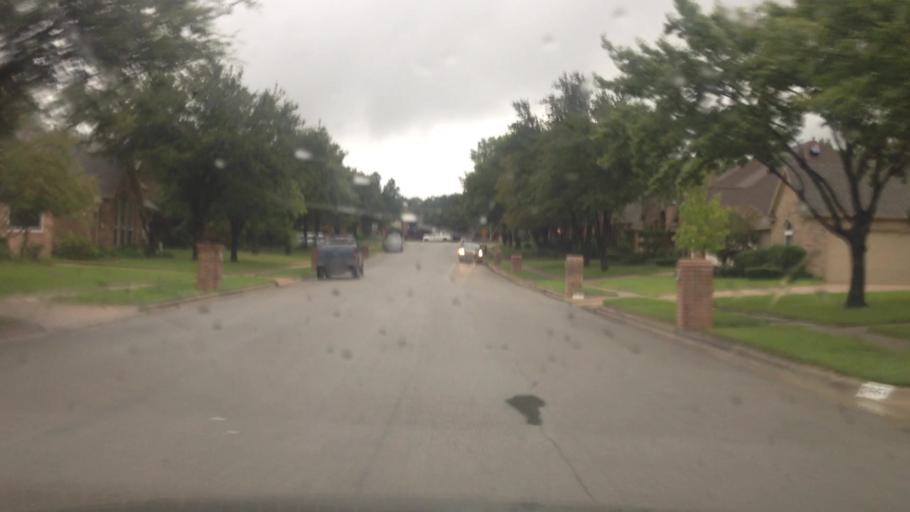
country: US
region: Texas
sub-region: Tarrant County
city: Colleyville
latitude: 32.8700
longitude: -97.1736
